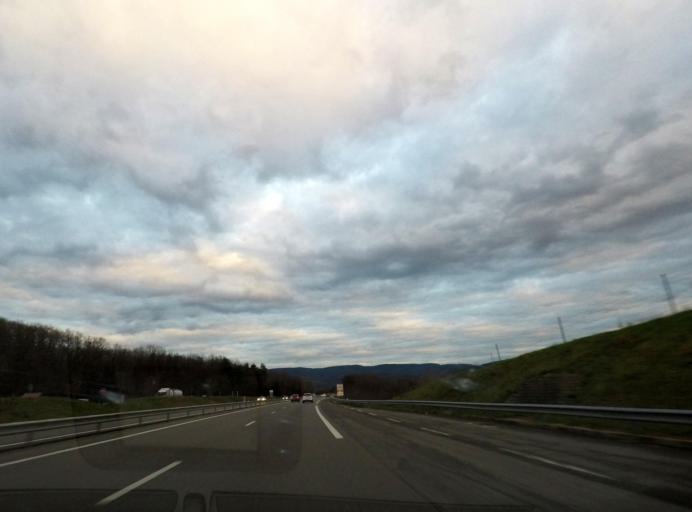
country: FR
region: Rhone-Alpes
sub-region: Departement de l'Ain
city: Neuville-sur-Ain
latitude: 46.0880
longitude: 5.3785
